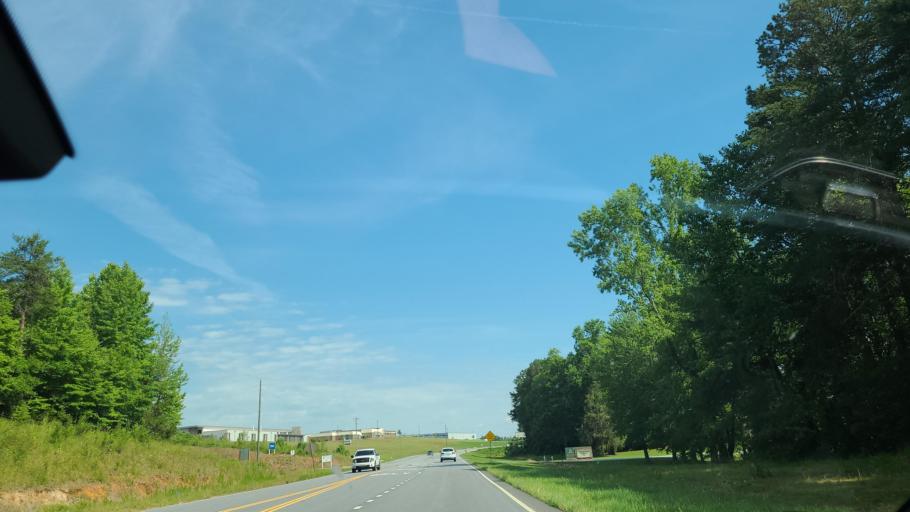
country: US
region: South Carolina
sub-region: Oconee County
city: Westminster
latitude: 34.6950
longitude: -83.0484
